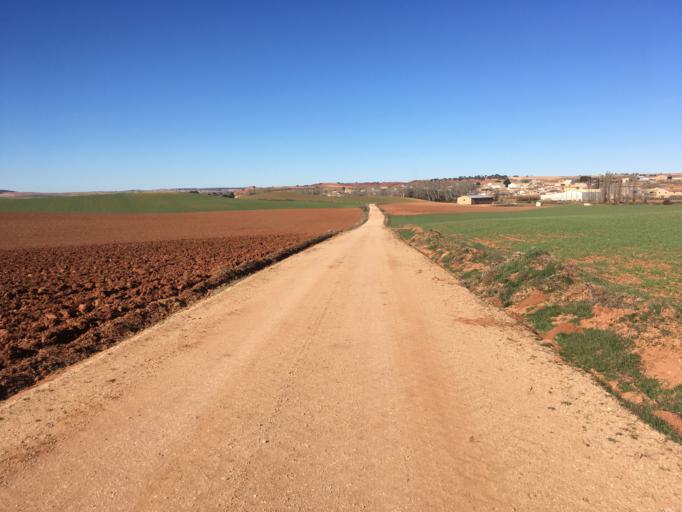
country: ES
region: Castille-La Mancha
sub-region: Provincia de Cuenca
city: Atalaya del Canavate
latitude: 39.5422
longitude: -2.2437
